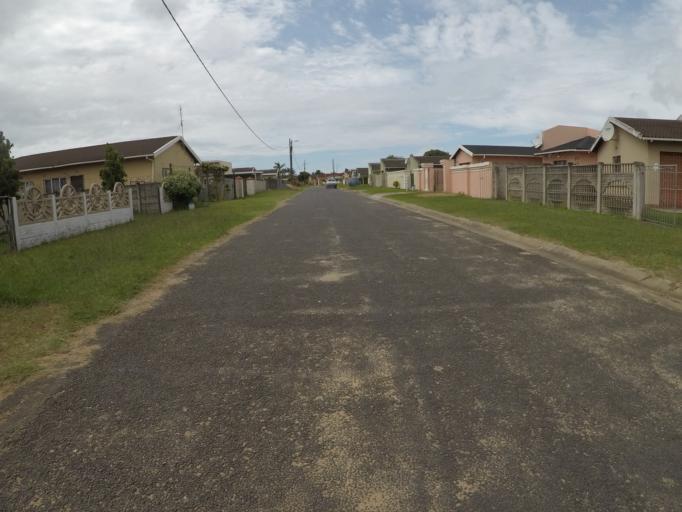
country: ZA
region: KwaZulu-Natal
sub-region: uThungulu District Municipality
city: eSikhawini
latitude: -28.8603
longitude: 31.9200
